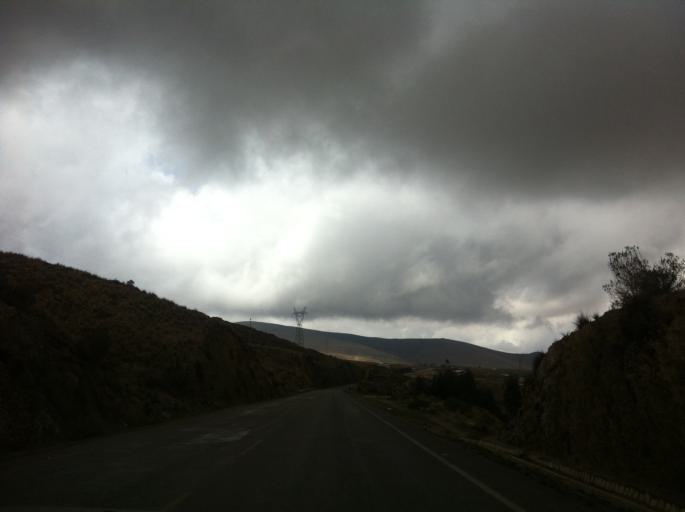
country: BO
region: Cochabamba
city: Irpa Irpa
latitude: -17.6955
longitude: -66.5176
